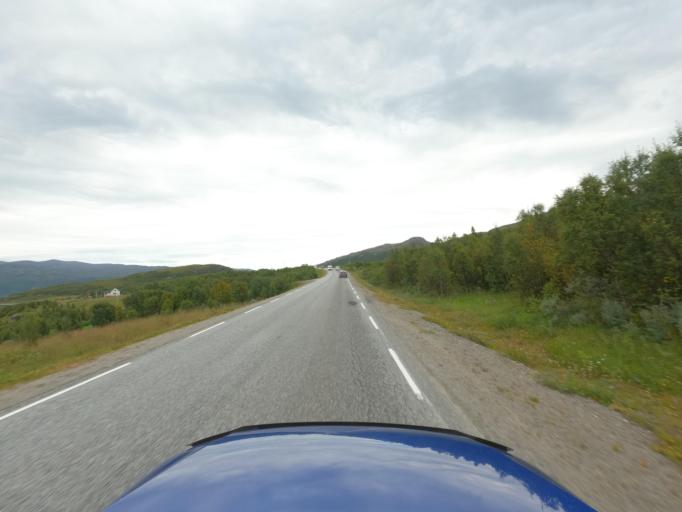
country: NO
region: Finnmark Fylke
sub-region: Kvalsund
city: Kvalsund
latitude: 70.4853
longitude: 24.1781
